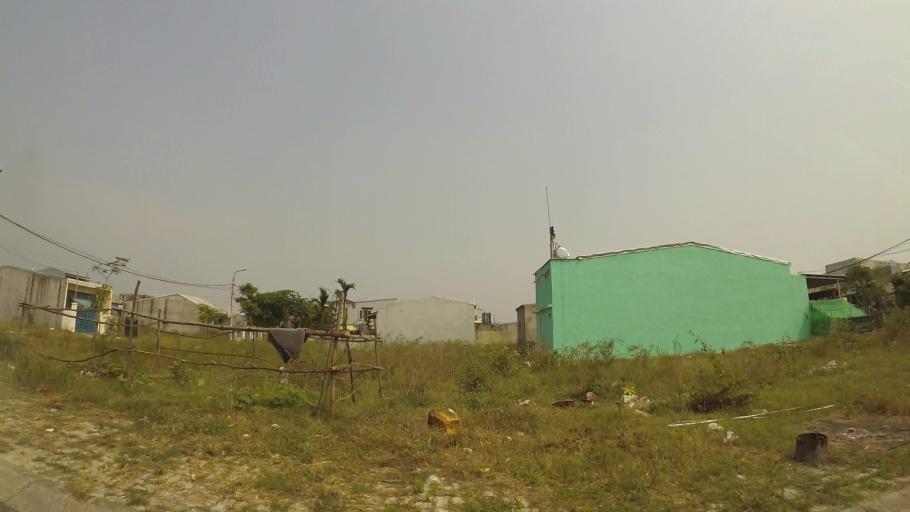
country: VN
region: Da Nang
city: Cam Le
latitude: 15.9702
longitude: 108.2127
